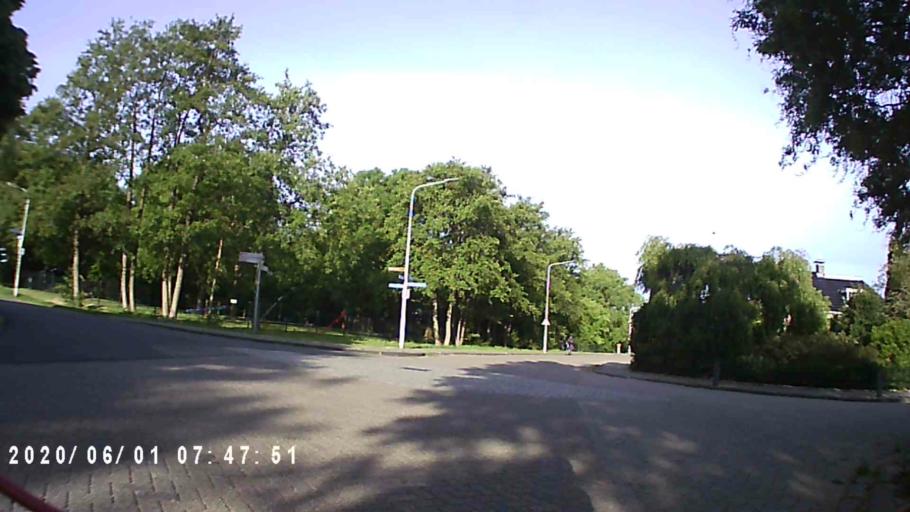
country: NL
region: Friesland
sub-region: Gemeente Dantumadiel
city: Rinsumageast
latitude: 53.2959
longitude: 5.9522
